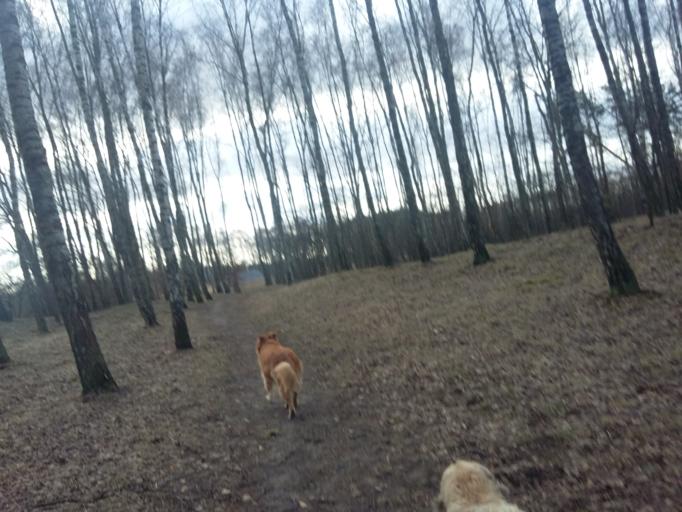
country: PL
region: Lodz Voivodeship
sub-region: Powiat pabianicki
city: Ksawerow
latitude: 51.7278
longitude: 19.4182
